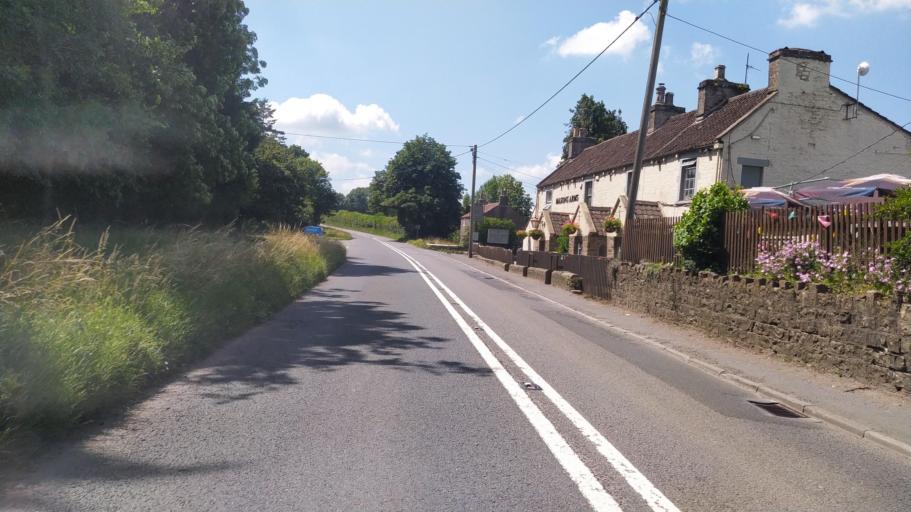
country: GB
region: England
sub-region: Somerset
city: Frome
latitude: 51.2155
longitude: -2.3366
